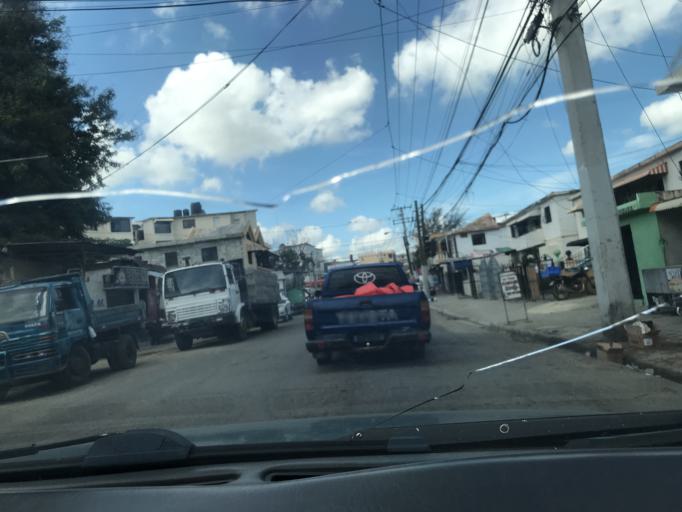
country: DO
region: Santiago
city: Palmar Arriba
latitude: 19.4868
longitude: -70.7419
